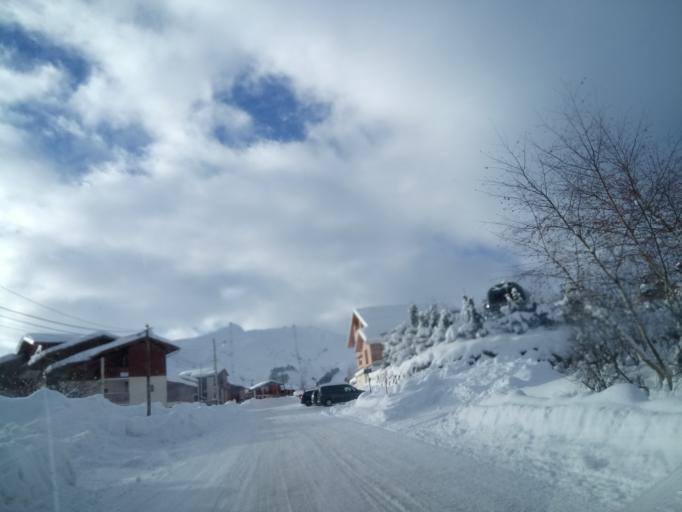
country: FR
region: Rhone-Alpes
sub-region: Departement de la Savoie
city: Saint-Jean-de-Maurienne
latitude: 45.2570
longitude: 6.2675
